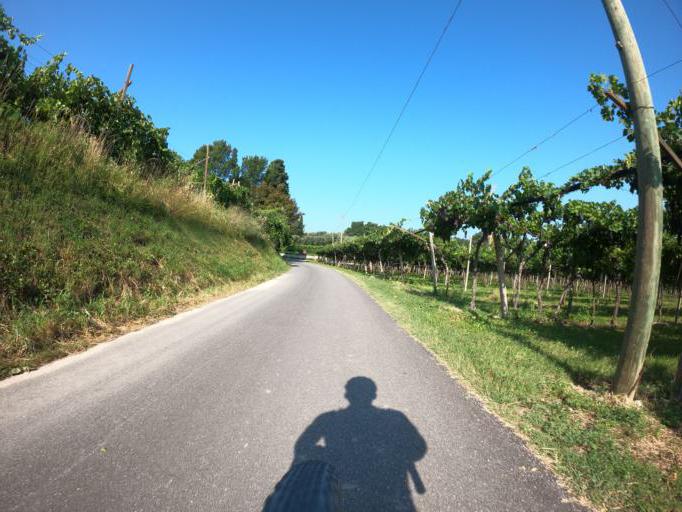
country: IT
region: Veneto
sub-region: Provincia di Verona
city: Calmasino
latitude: 45.5049
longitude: 10.7571
